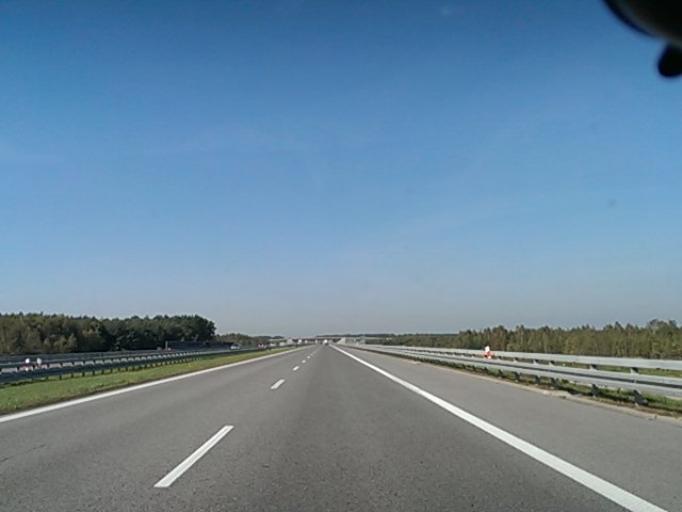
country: PL
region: Subcarpathian Voivodeship
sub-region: Powiat rzeszowski
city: Trzciana
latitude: 50.1135
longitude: 21.8290
